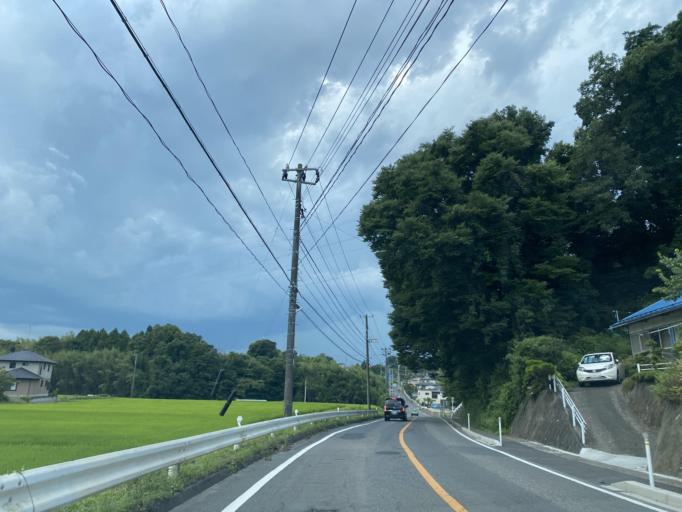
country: JP
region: Fukushima
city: Koriyama
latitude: 37.4086
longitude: 140.4159
